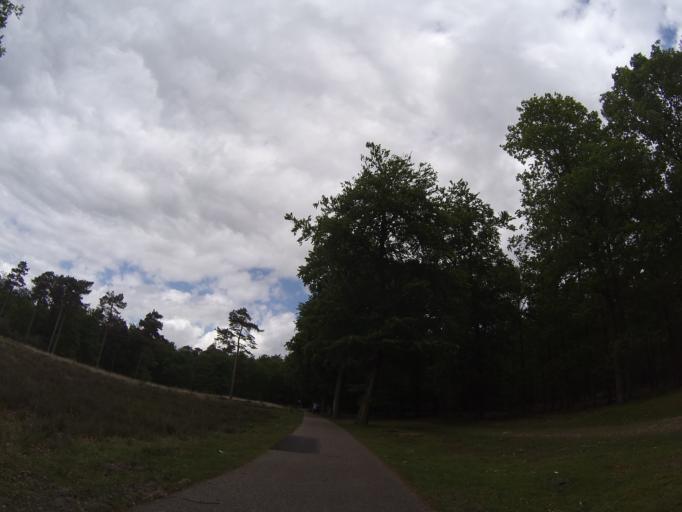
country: NL
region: Drenthe
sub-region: Gemeente Borger-Odoorn
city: Borger
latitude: 52.8683
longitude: 6.8130
